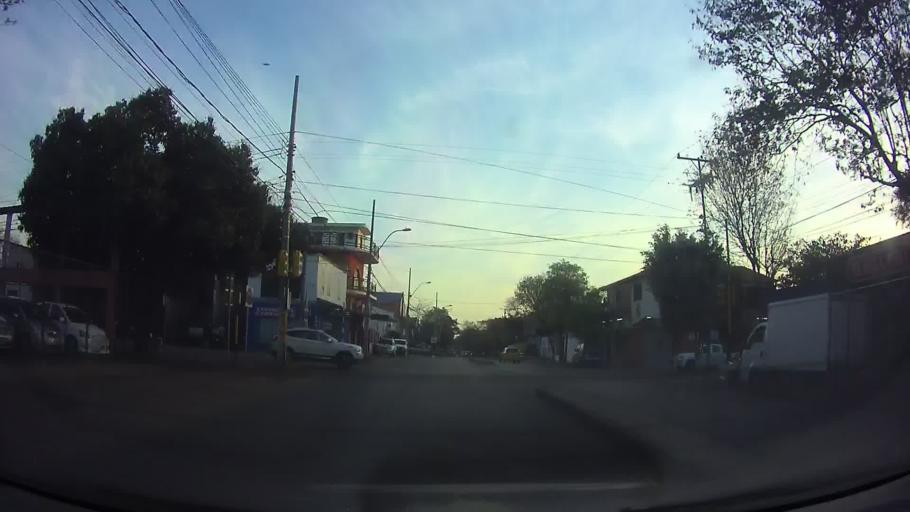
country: PY
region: Central
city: Lambare
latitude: -25.3189
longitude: -57.5762
